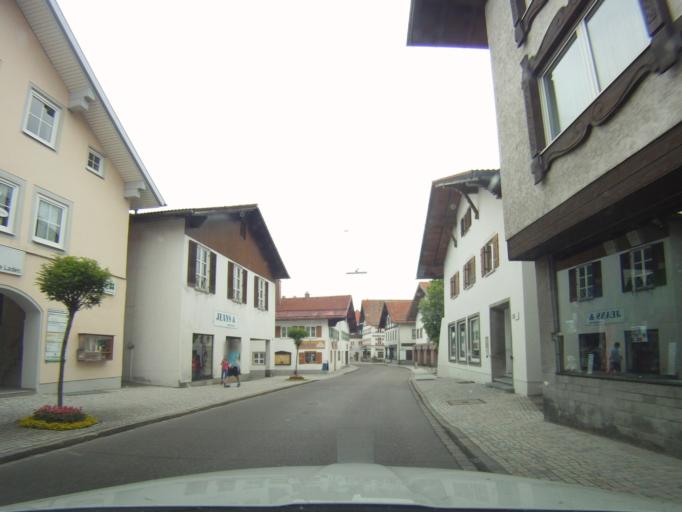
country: DE
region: Bavaria
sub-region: Swabia
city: Nesselwang
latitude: 47.6218
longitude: 10.5000
